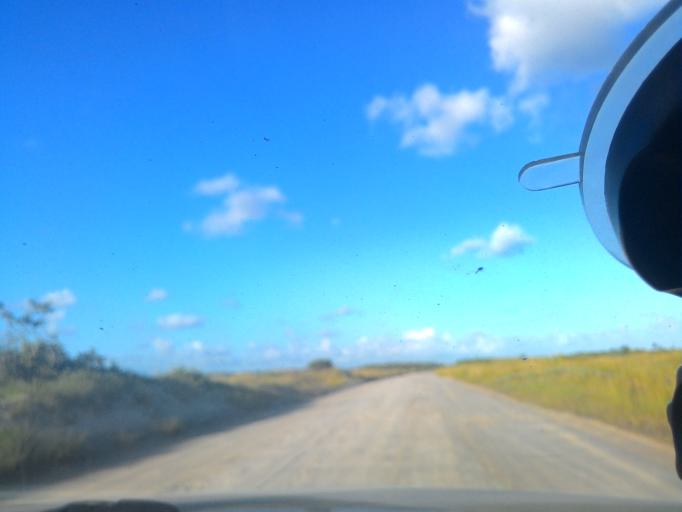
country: BR
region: Sao Paulo
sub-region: Pariquera-Acu
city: Pariquera Acu
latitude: -24.8789
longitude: -47.7349
